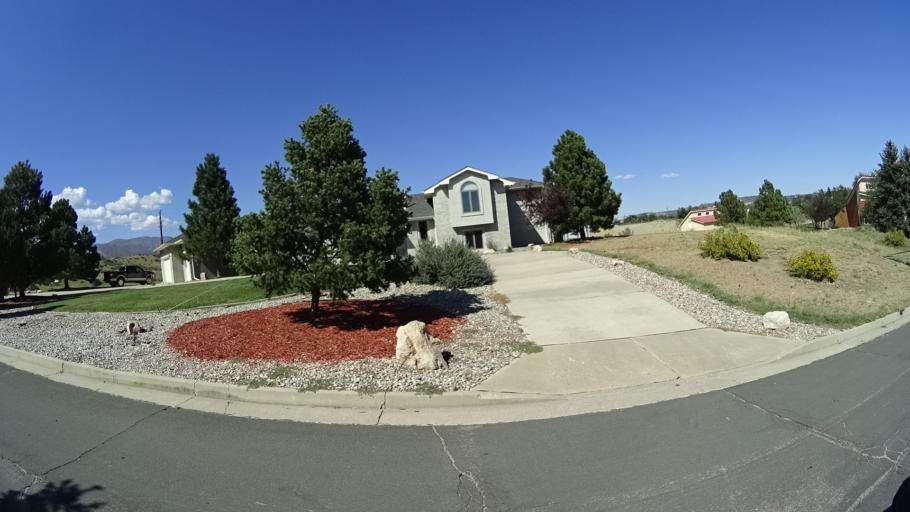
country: US
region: Colorado
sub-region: El Paso County
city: Colorado Springs
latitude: 38.8620
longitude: -104.8433
